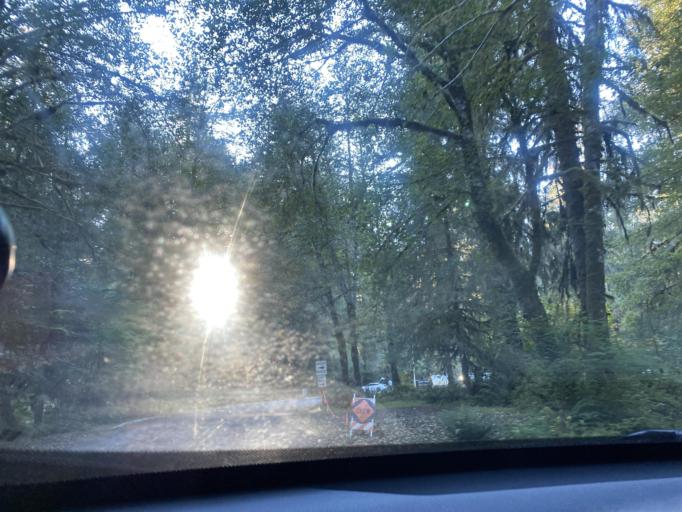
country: US
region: Washington
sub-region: Clallam County
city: Forks
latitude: 47.8608
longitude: -123.9356
